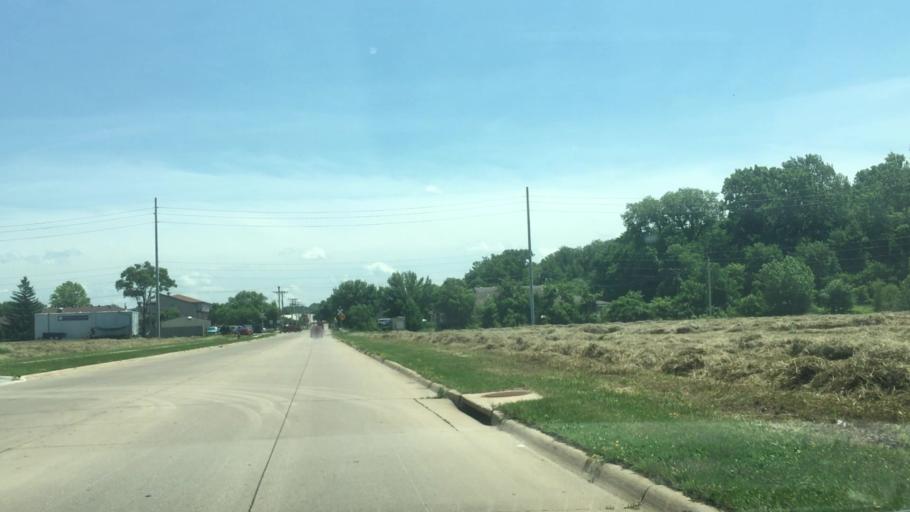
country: US
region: Iowa
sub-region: Johnson County
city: Iowa City
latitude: 41.6406
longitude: -91.5329
